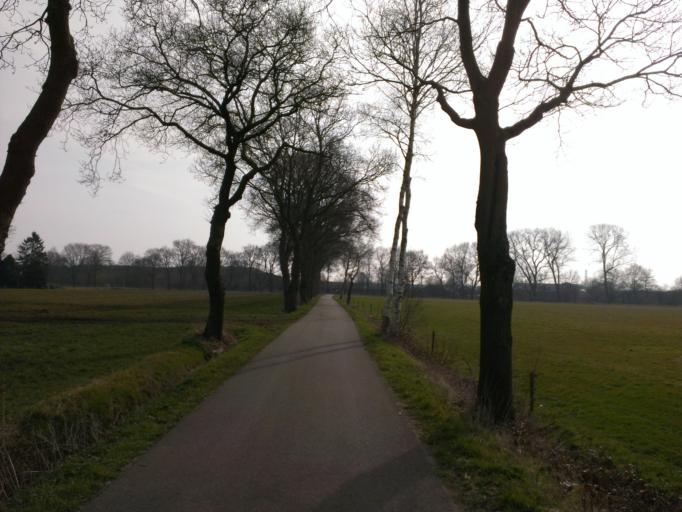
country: NL
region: Drenthe
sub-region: Gemeente Hoogeveen
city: Hoogeveen
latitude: 52.7409
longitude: 6.5129
